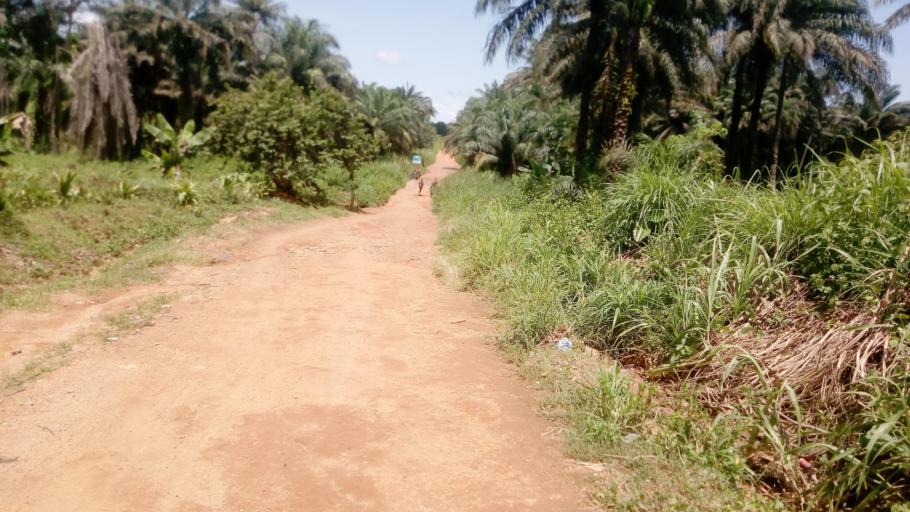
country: SL
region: Northern Province
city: Binkolo
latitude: 8.9569
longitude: -11.9641
